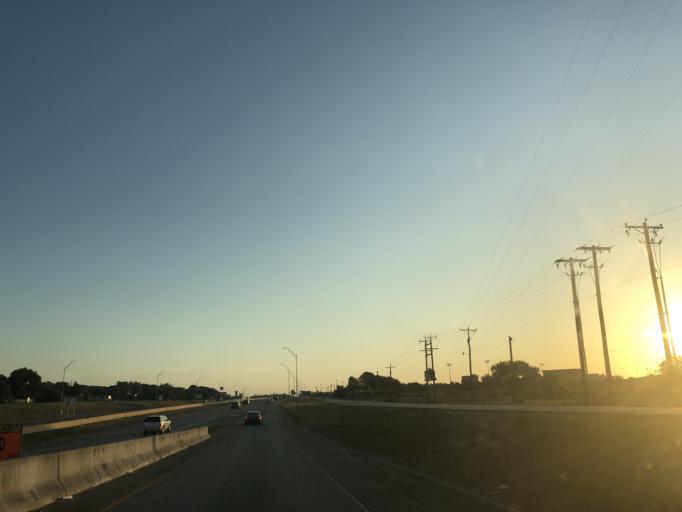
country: US
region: Texas
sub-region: Dallas County
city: Cedar Hill
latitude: 32.5795
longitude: -96.9564
